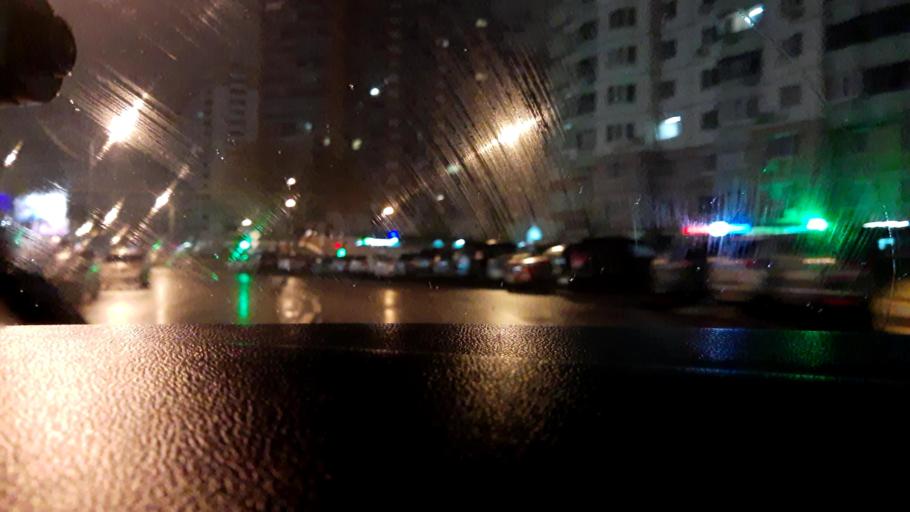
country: RU
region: Moskovskaya
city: Pavshino
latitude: 55.8204
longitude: 37.3701
